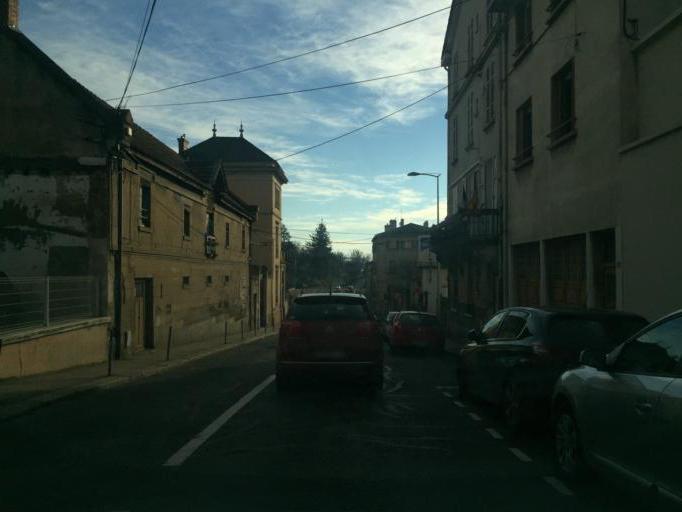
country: FR
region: Rhone-Alpes
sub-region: Departement du Rhone
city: Villefranche-sur-Saone
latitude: 45.9903
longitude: 4.7217
